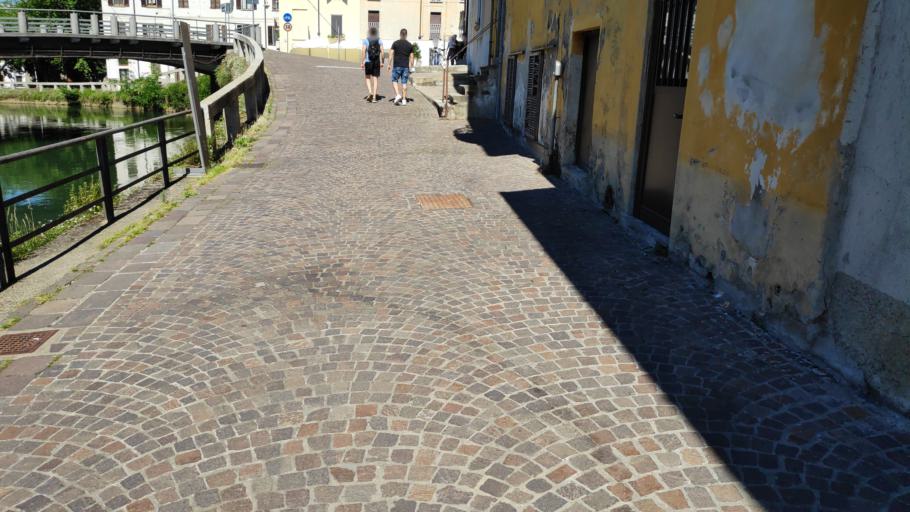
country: IT
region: Lombardy
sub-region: Citta metropolitana di Milano
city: Gorgonzola
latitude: 45.5301
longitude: 9.4085
